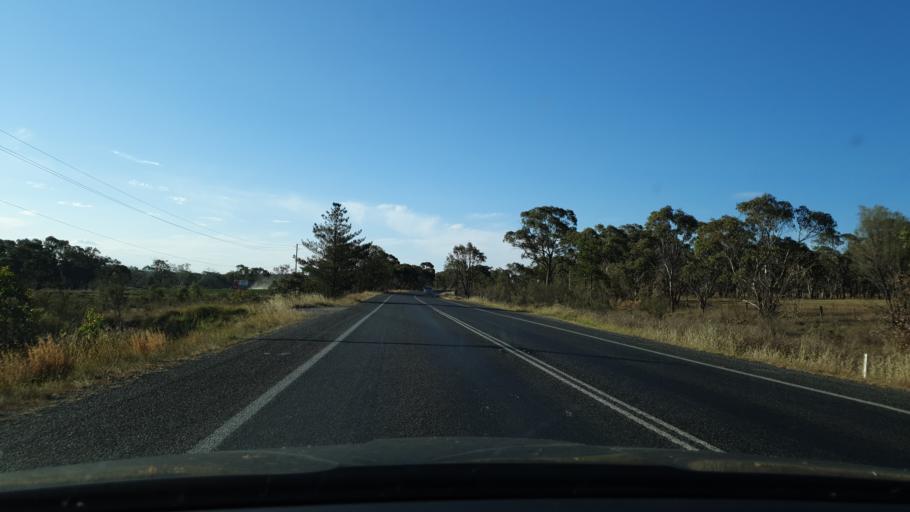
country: AU
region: Queensland
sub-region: Southern Downs
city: Stanthorpe
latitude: -28.6713
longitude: 151.9181
